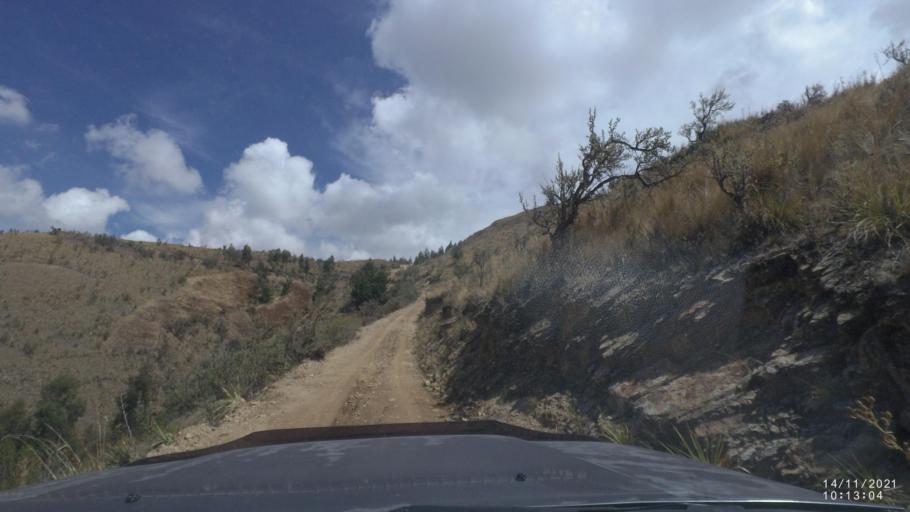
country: BO
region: Cochabamba
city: Cochabamba
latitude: -17.3447
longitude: -66.0860
